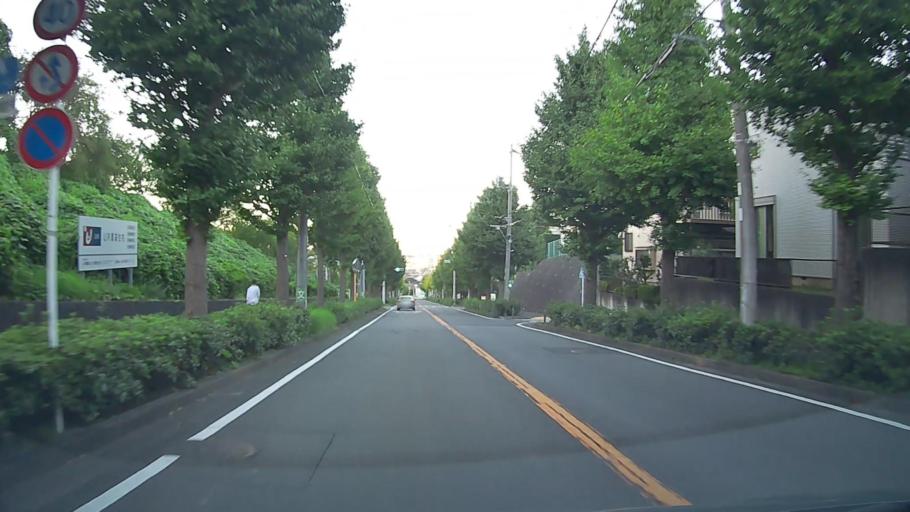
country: JP
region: Tokyo
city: Chofugaoka
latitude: 35.6264
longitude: 139.5272
